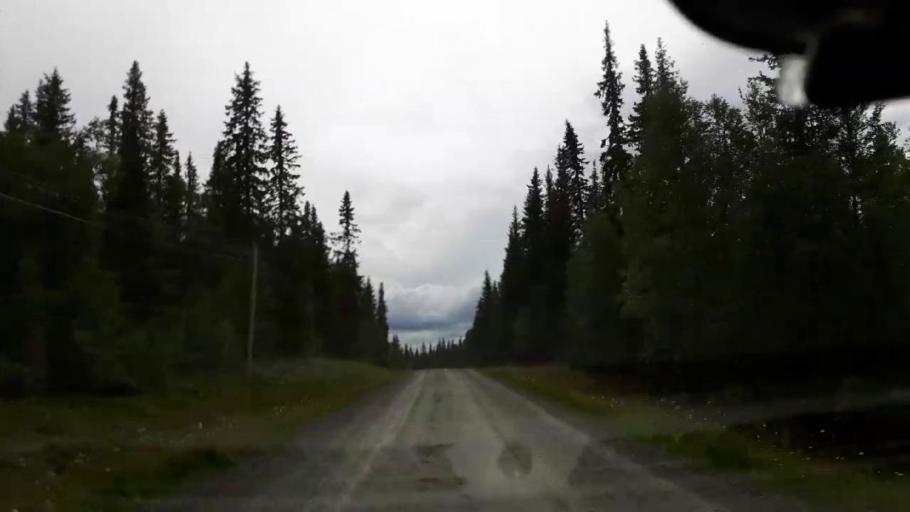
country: SE
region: Jaemtland
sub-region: Krokoms Kommun
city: Valla
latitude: 63.7416
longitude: 13.8372
